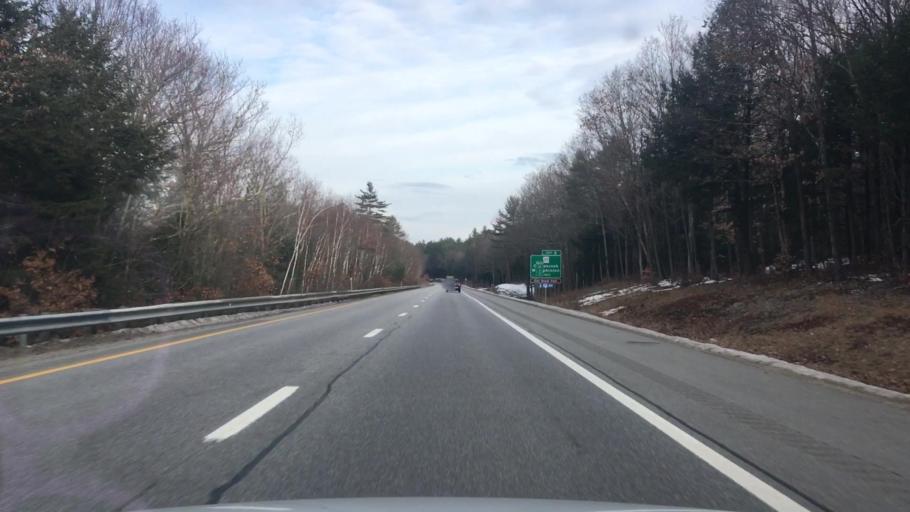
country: US
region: New Hampshire
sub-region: Merrimack County
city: Hopkinton
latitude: 43.1892
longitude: -71.6988
